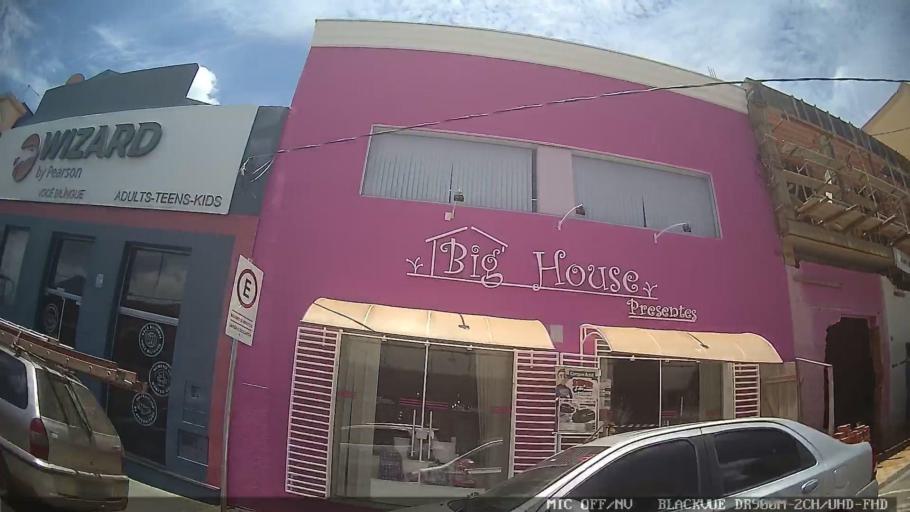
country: BR
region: Sao Paulo
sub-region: Laranjal Paulista
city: Laranjal Paulista
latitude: -23.0492
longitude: -47.8361
